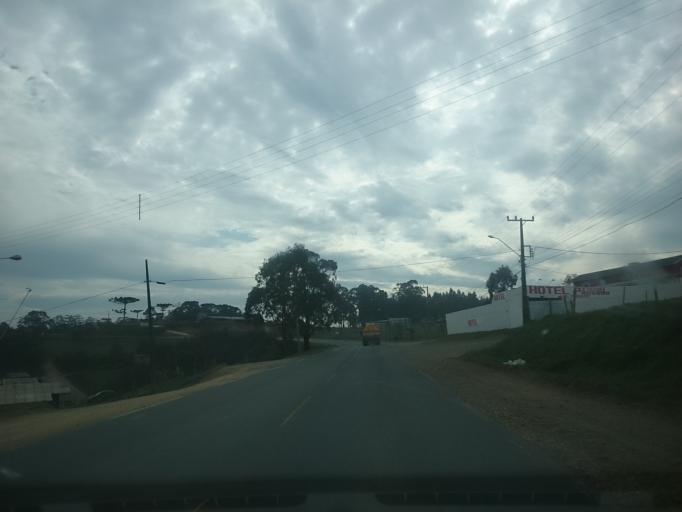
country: BR
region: Santa Catarina
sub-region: Lages
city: Lages
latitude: -27.7770
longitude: -50.3202
